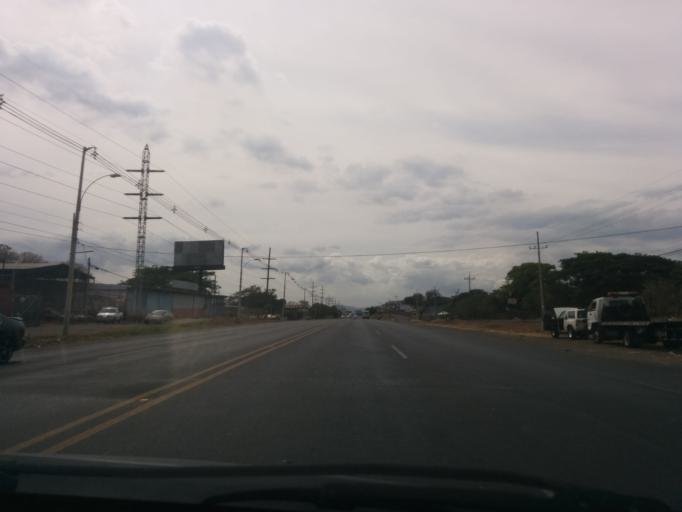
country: CR
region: Alajuela
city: Alajuela
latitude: 9.9947
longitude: -84.2348
